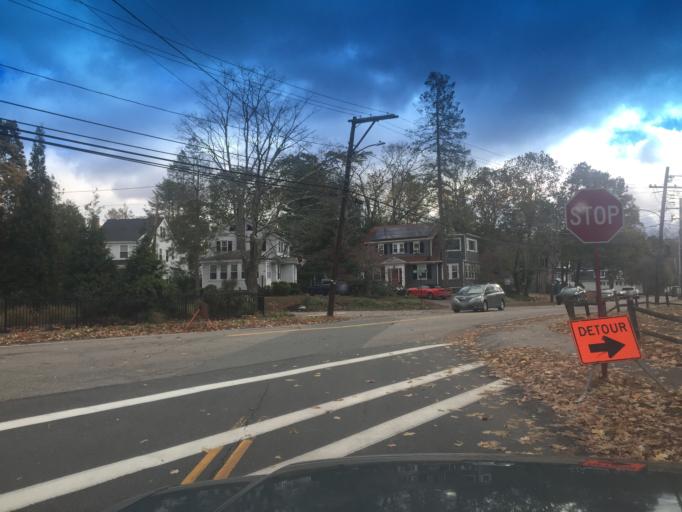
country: US
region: Massachusetts
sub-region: Norfolk County
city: Needham
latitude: 42.2775
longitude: -71.2324
